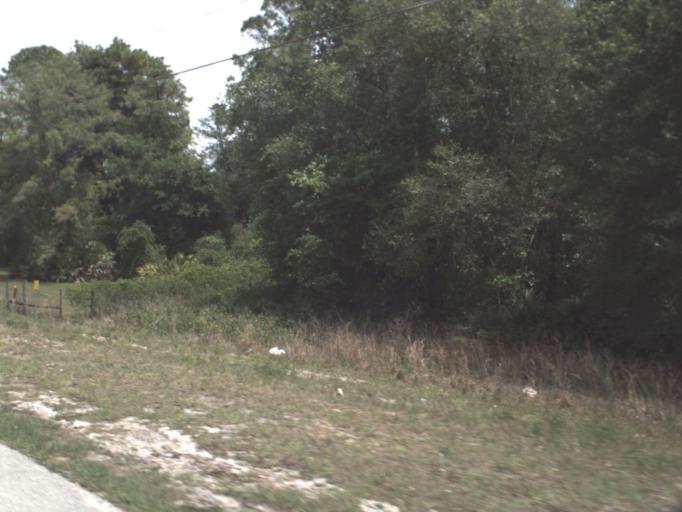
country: US
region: Florida
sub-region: Lake County
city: Lake Mack-Forest Hills
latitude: 28.9459
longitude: -81.4263
